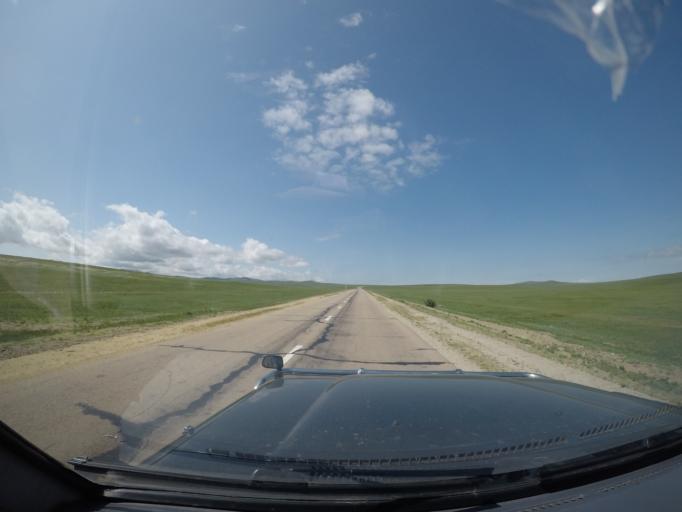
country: MN
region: Hentiy
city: Bayan
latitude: 47.2968
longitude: 111.2011
